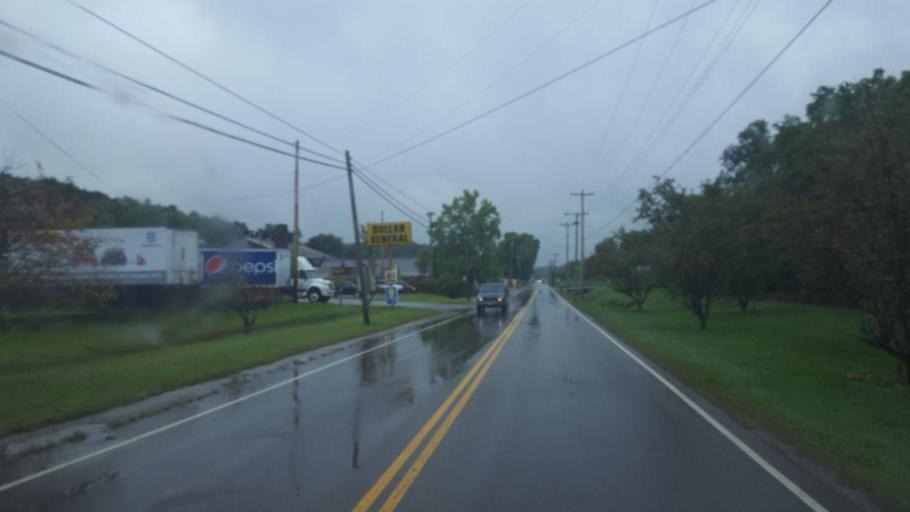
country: US
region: Ohio
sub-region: Jackson County
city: Oak Hill
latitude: 38.8930
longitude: -82.5737
